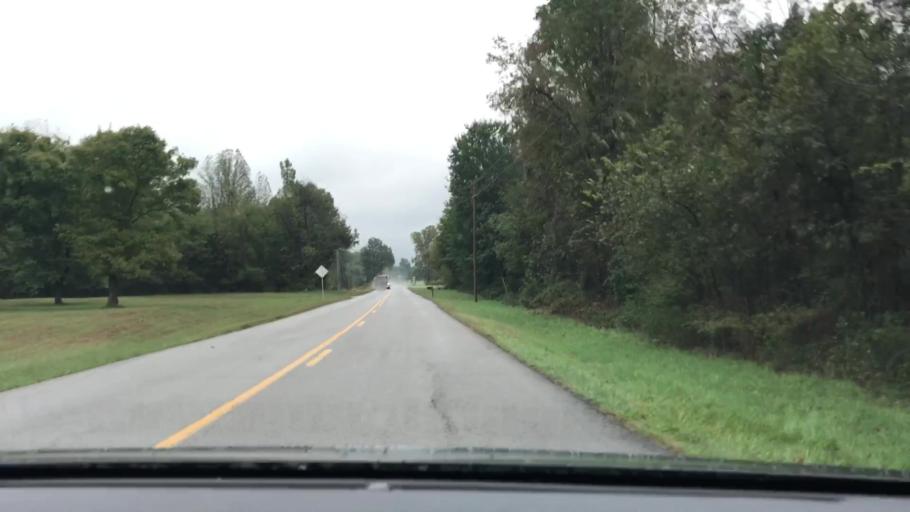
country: US
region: Kentucky
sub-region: McLean County
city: Calhoun
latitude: 37.4746
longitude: -87.2432
